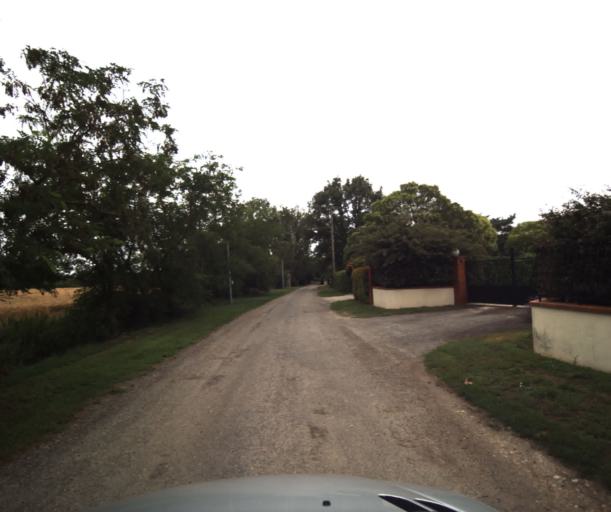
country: FR
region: Midi-Pyrenees
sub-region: Departement de la Haute-Garonne
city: Labarthe-sur-Leze
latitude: 43.4699
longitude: 1.4023
